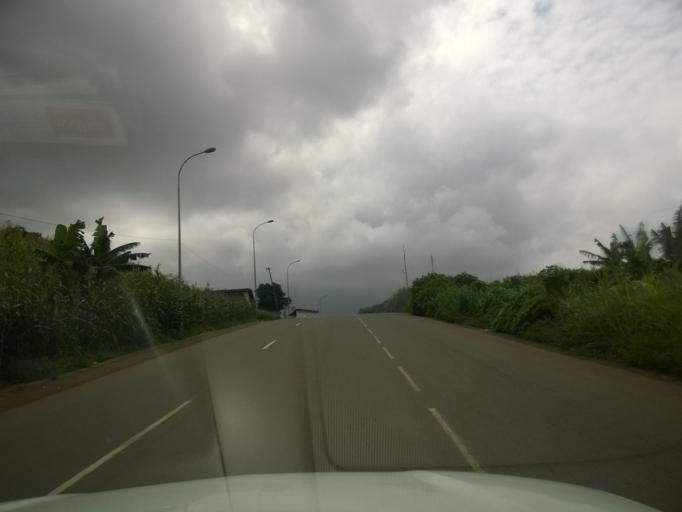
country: CM
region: Centre
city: Yaounde
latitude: 3.8504
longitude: 11.5040
